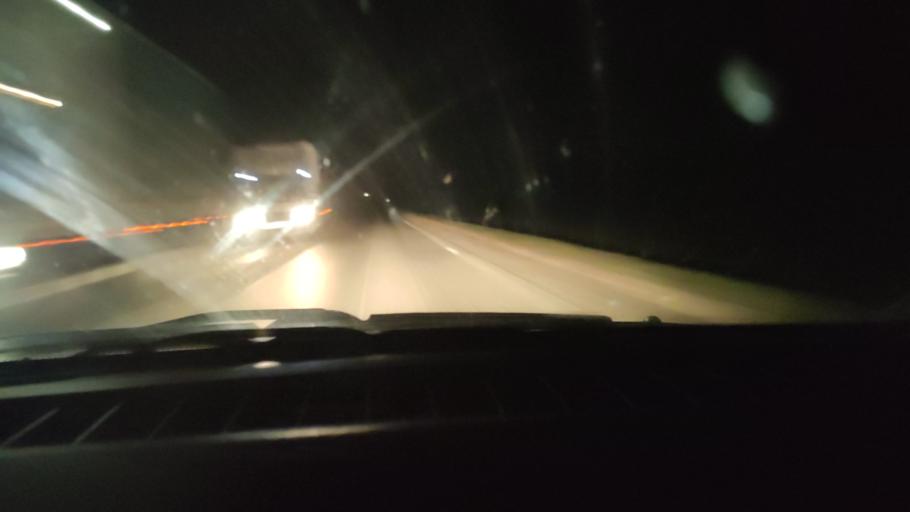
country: RU
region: Saratov
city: Dukhovnitskoye
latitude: 52.7065
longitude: 48.2609
